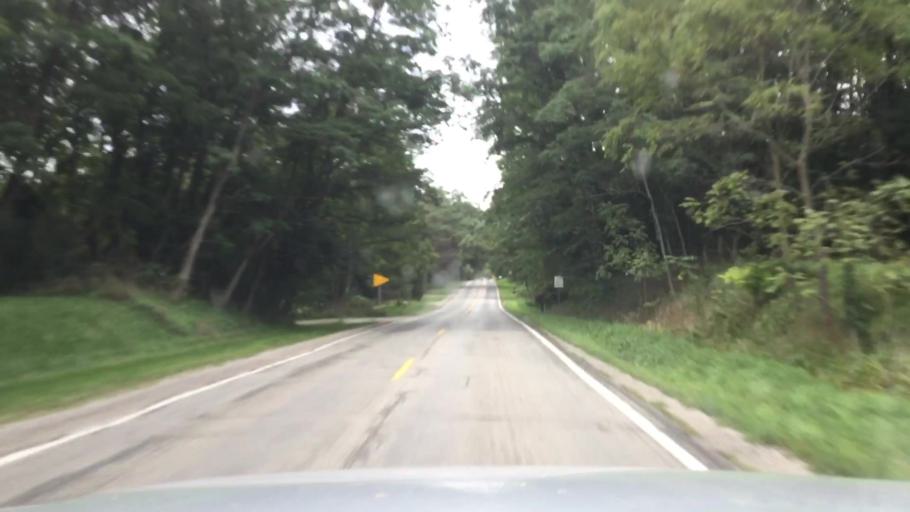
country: US
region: Michigan
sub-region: Genesee County
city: Argentine
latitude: 42.8134
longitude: -83.9048
